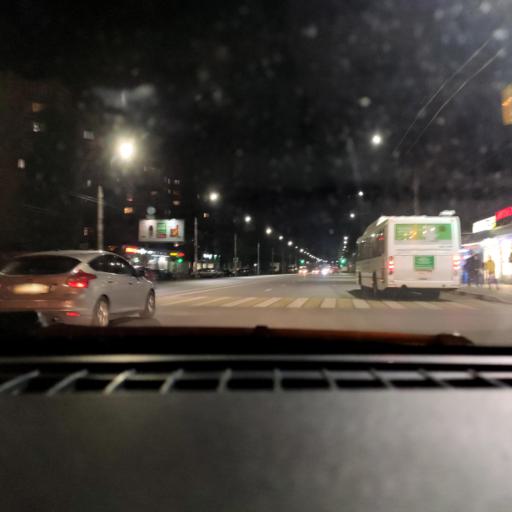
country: RU
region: Voronezj
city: Voronezh
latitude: 51.6841
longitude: 39.2629
